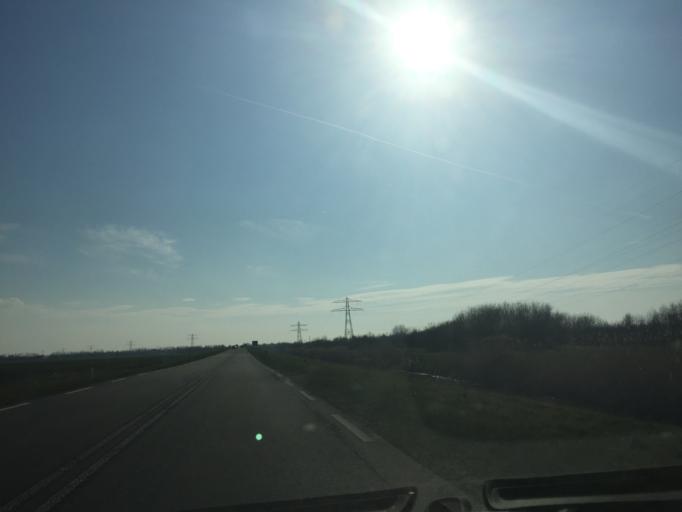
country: NL
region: South Holland
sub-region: Gemeente Hillegom
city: Hillegom
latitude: 52.2768
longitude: 4.5941
